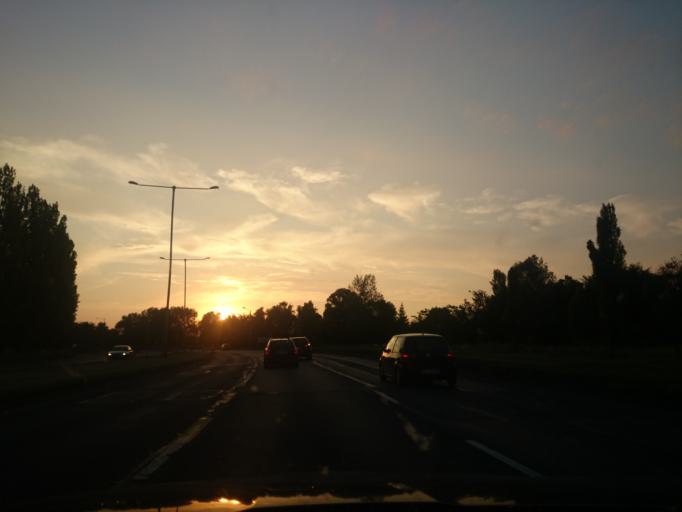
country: PL
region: West Pomeranian Voivodeship
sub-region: Szczecin
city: Szczecin
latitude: 53.3861
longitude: 14.6416
